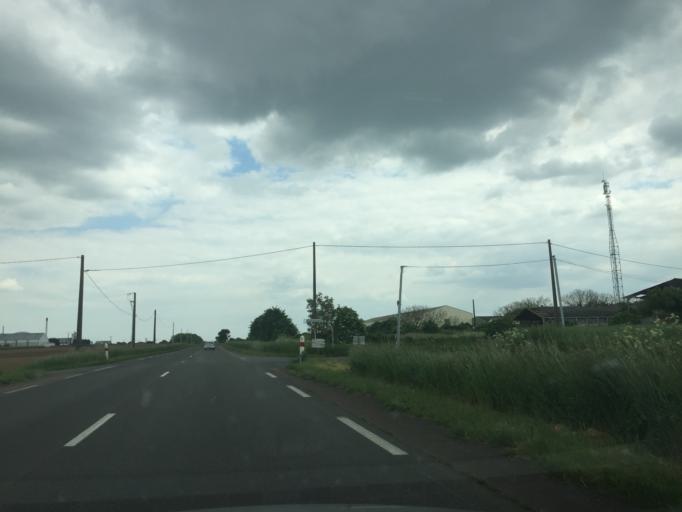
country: FR
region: Pays de la Loire
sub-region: Departement de la Vendee
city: Benet
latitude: 46.3865
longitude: -0.6237
